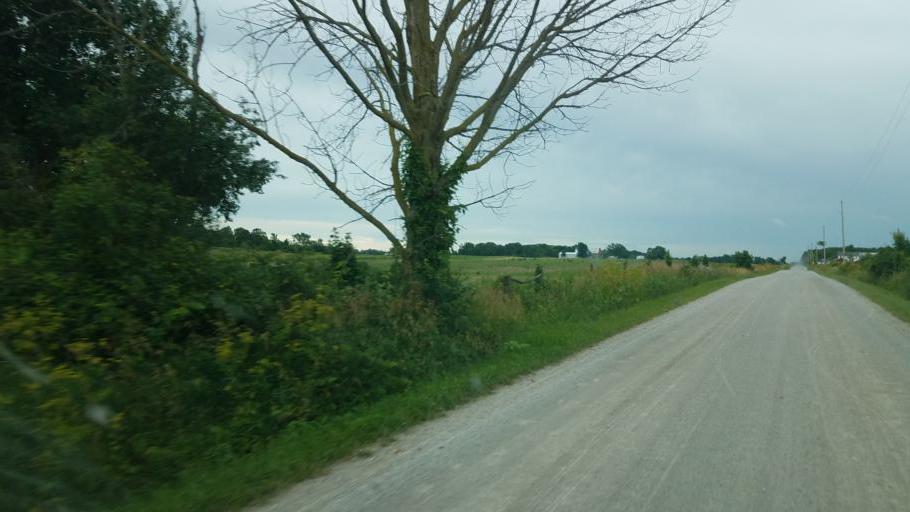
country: US
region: Ohio
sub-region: Huron County
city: Greenwich
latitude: 40.9390
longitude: -82.4313
